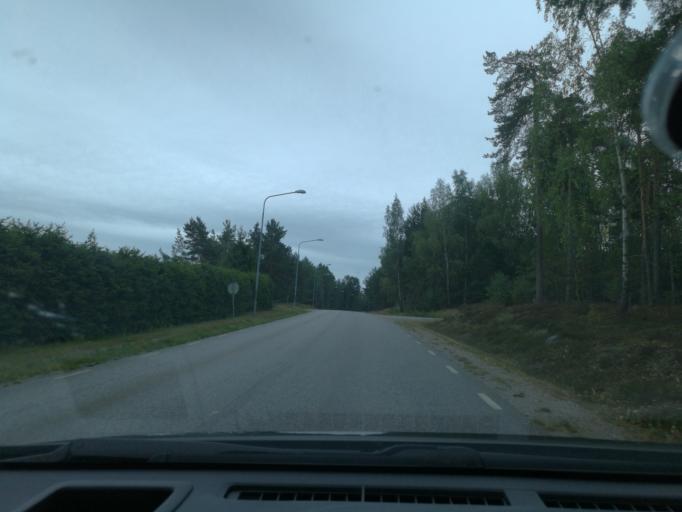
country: SE
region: Vaestmanland
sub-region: Kungsors Kommun
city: Kungsoer
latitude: 59.4127
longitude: 16.1063
